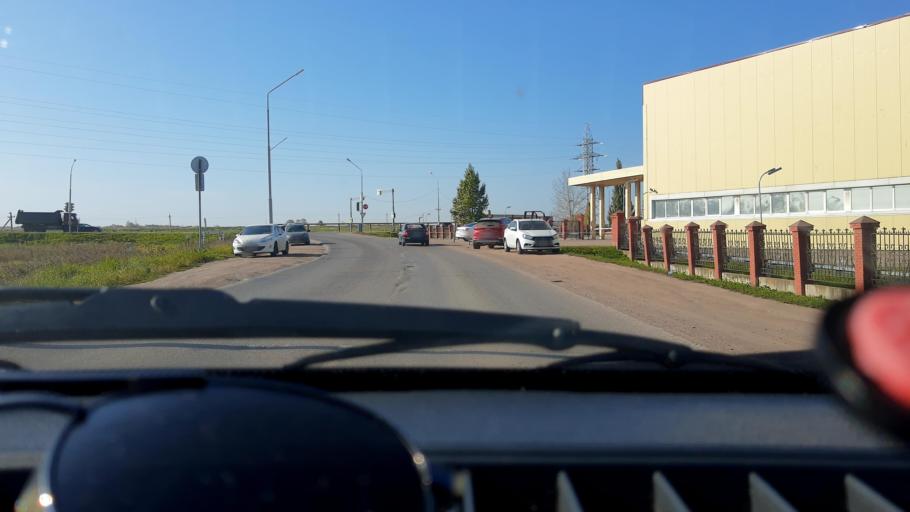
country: RU
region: Bashkortostan
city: Mikhaylovka
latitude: 54.8328
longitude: 55.8174
